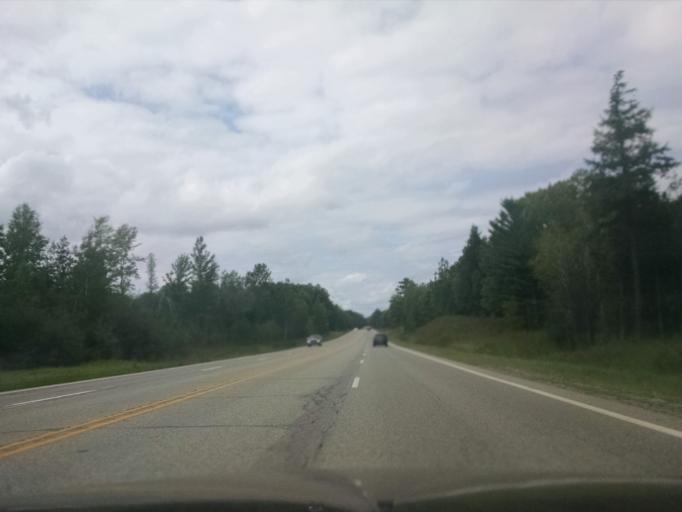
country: US
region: Michigan
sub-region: Osceola County
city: Evart
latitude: 44.0531
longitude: -85.1797
